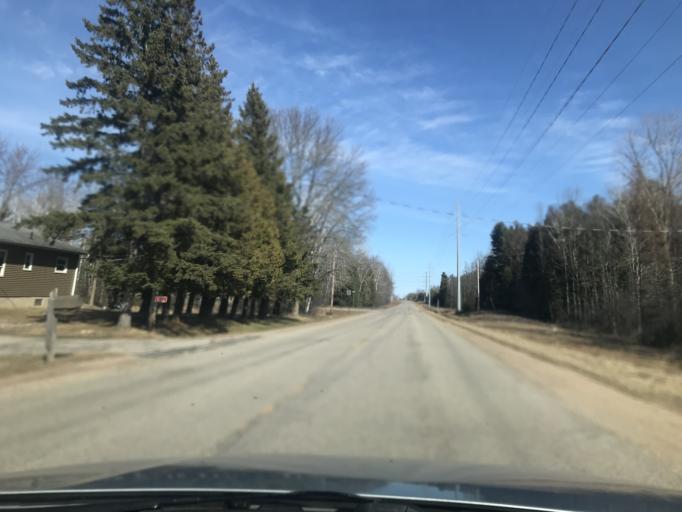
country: US
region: Wisconsin
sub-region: Marinette County
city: Marinette
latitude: 45.1449
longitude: -87.6450
